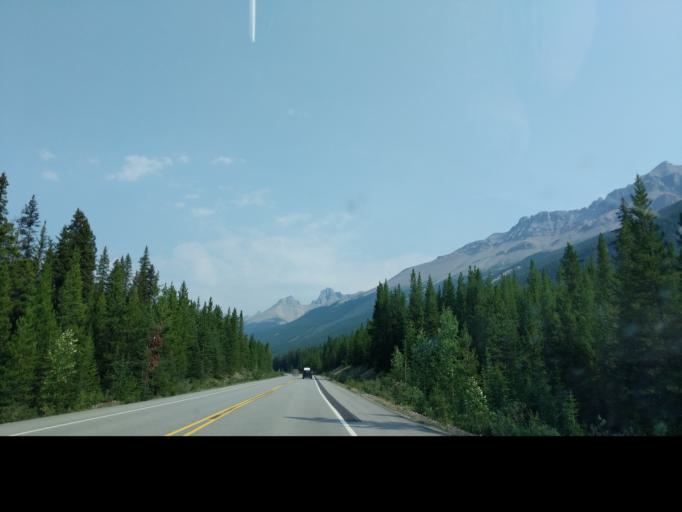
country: CA
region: Alberta
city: Lake Louise
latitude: 51.8010
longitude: -116.5793
